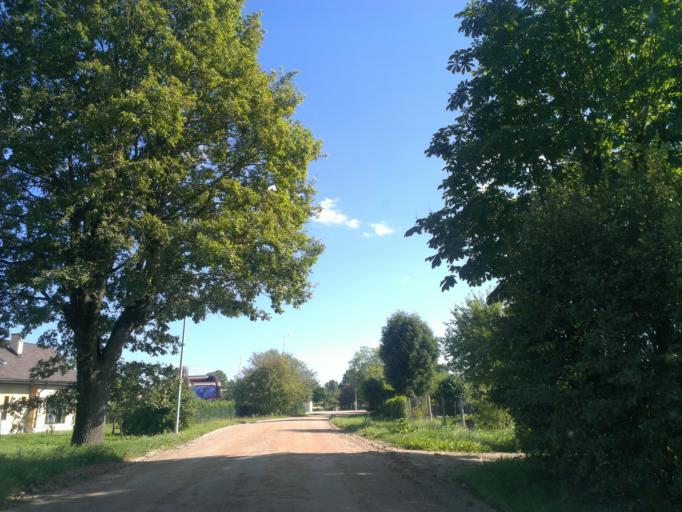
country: LV
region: Sigulda
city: Sigulda
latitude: 57.1634
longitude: 24.8874
